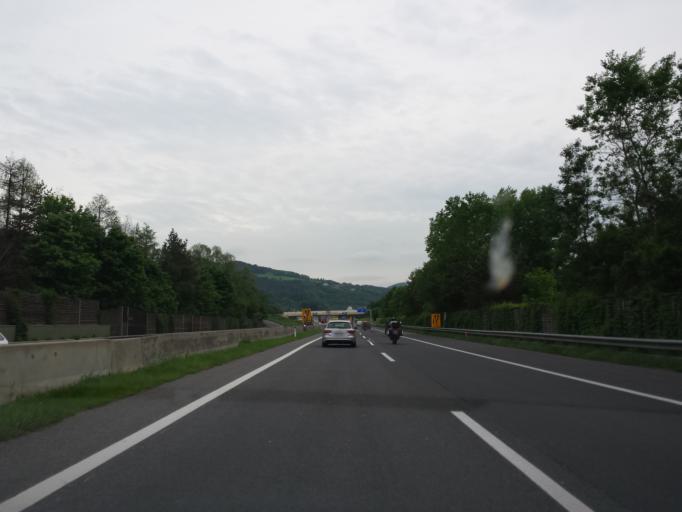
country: AT
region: Lower Austria
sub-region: Politischer Bezirk Neunkirchen
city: Warth
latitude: 47.6363
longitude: 16.1268
